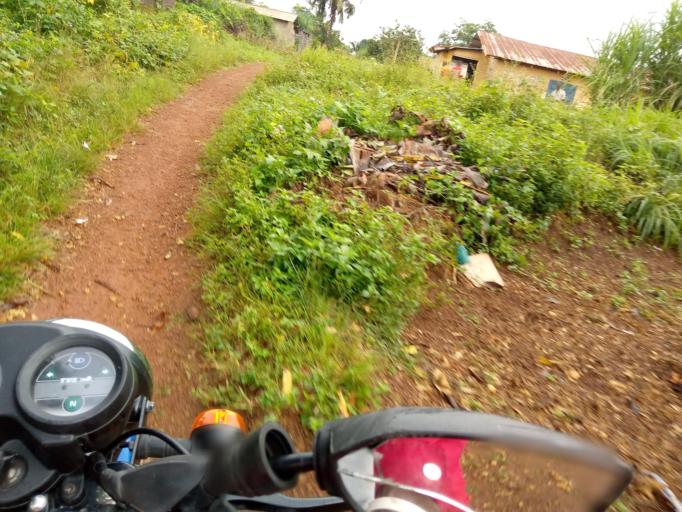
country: SL
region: Eastern Province
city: Buedu
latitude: 8.4636
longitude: -10.3400
